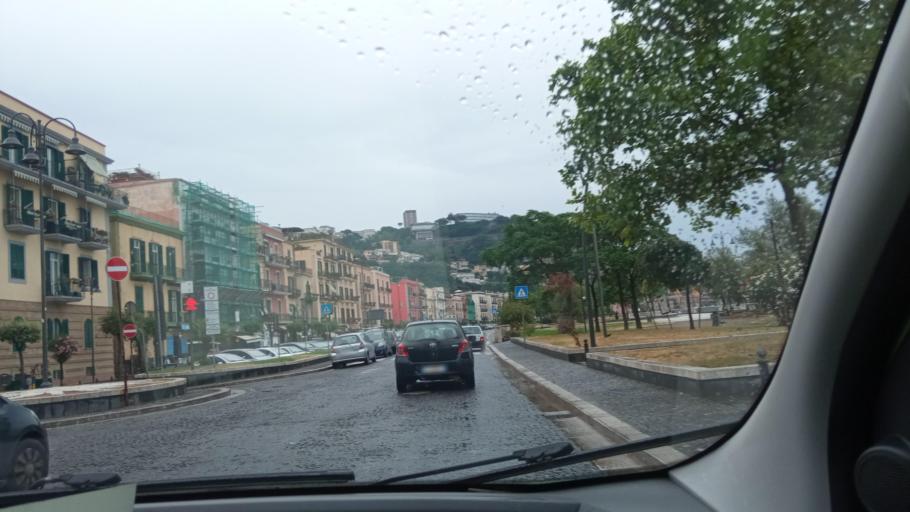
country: IT
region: Campania
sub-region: Provincia di Napoli
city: Pozzuoli
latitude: 40.8213
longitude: 14.1275
